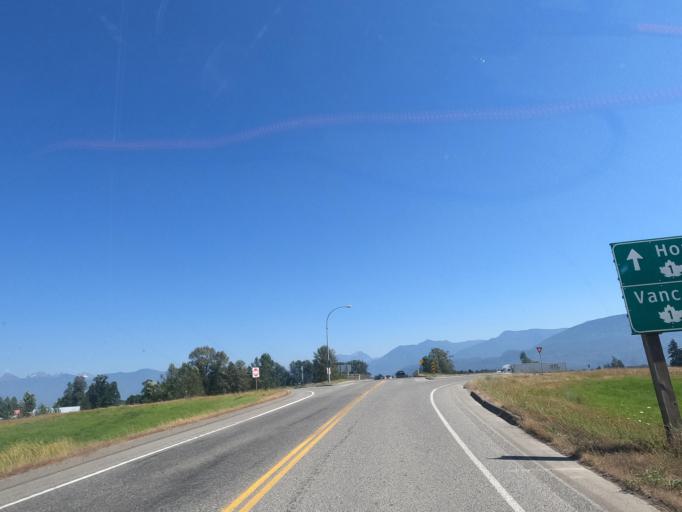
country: CA
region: British Columbia
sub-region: Fraser Valley Regional District
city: Chilliwack
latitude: 49.1303
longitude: -122.0826
